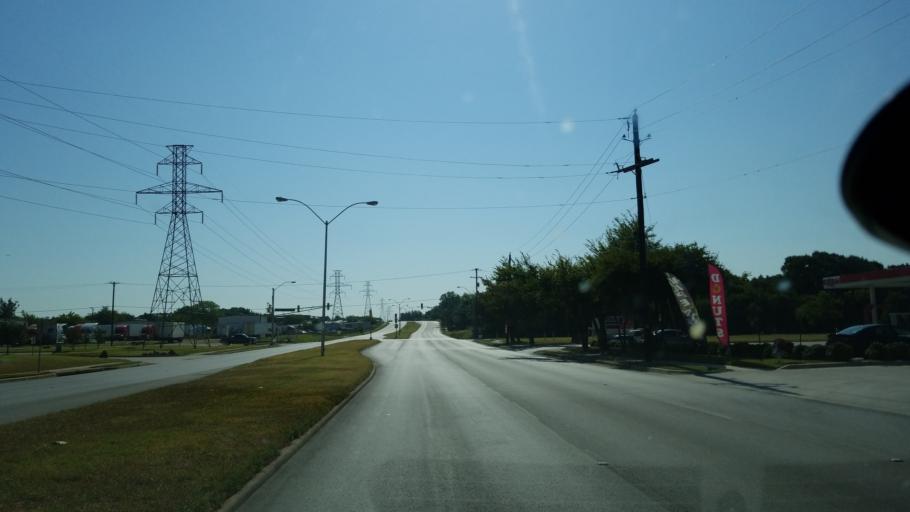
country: US
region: Texas
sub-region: Tarrant County
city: Euless
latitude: 32.8196
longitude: -97.0837
